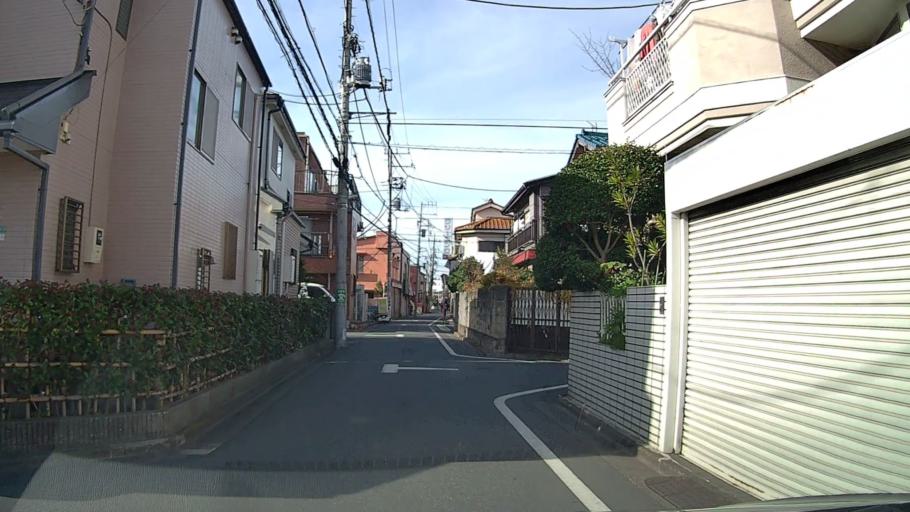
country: JP
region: Saitama
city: Wako
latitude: 35.7347
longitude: 139.6208
